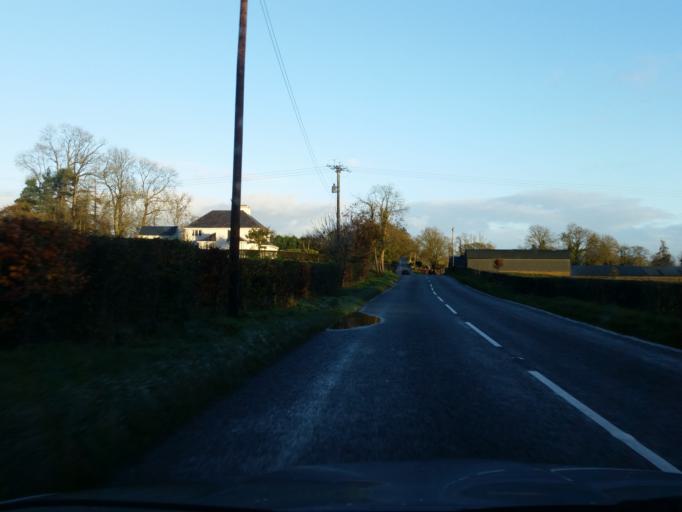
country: IE
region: Ulster
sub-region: An Cabhan
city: Ballyconnell
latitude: 54.1910
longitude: -7.5546
